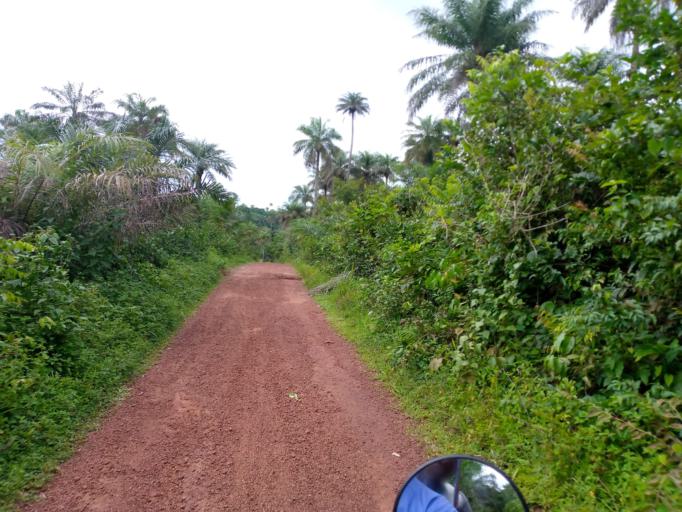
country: SL
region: Northern Province
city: Mange
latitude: 8.9799
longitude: -12.7116
